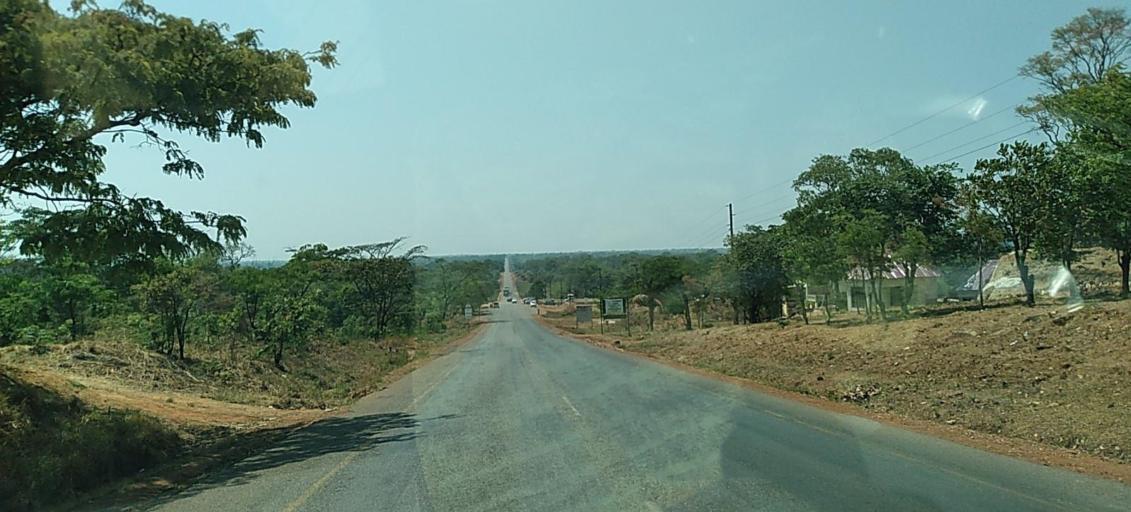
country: ZM
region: North-Western
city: Solwezi
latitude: -12.3331
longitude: 25.8941
